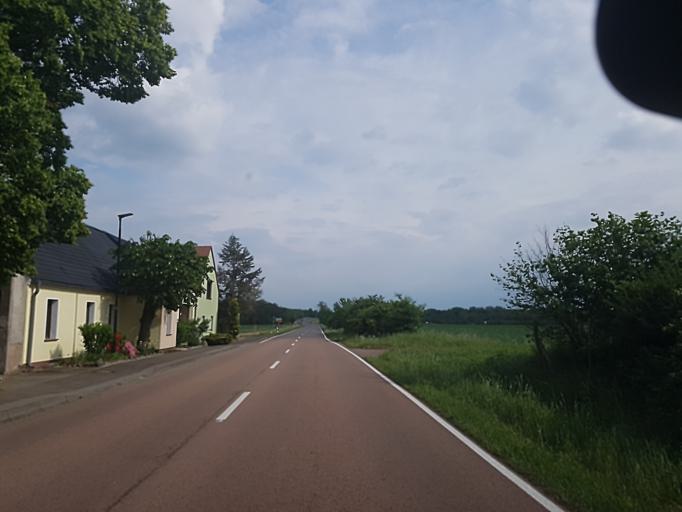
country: DE
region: Saxony-Anhalt
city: Coswig
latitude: 51.9106
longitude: 12.4133
